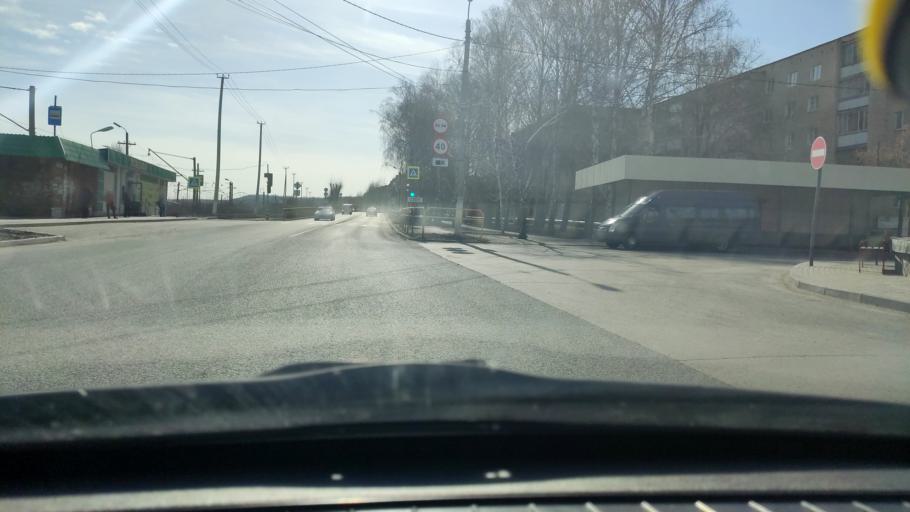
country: RU
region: Samara
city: Zhigulevsk
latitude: 53.4059
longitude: 49.4918
